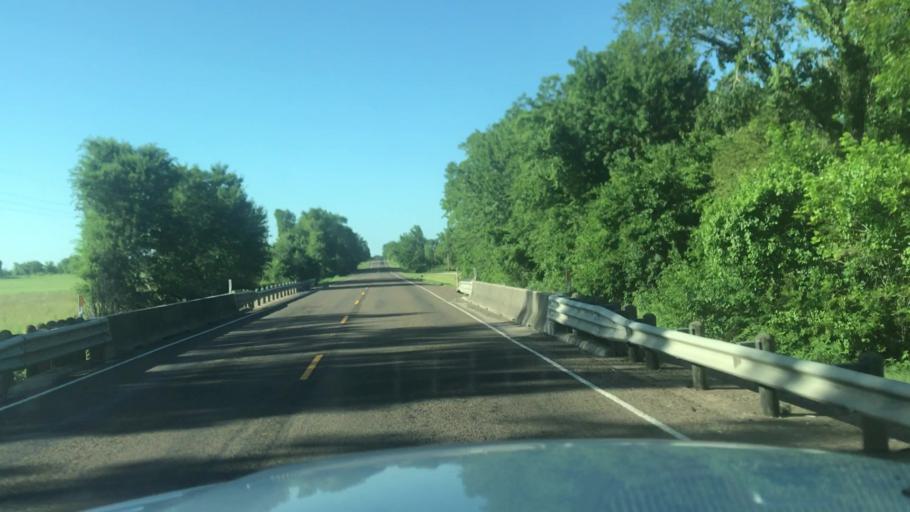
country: US
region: Texas
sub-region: Grimes County
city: Anderson
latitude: 30.6196
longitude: -95.8848
